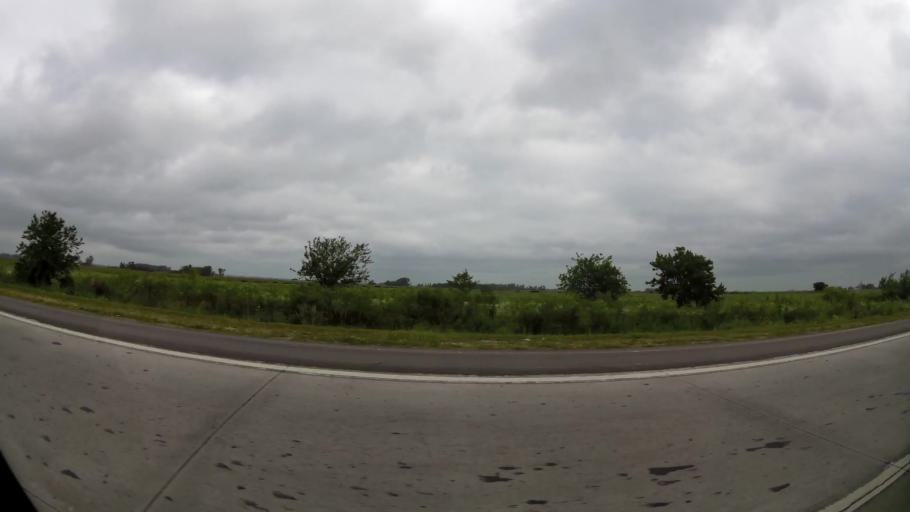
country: AR
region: Buenos Aires
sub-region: Partido de San Vicente
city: San Vicente
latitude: -35.0204
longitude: -58.3137
